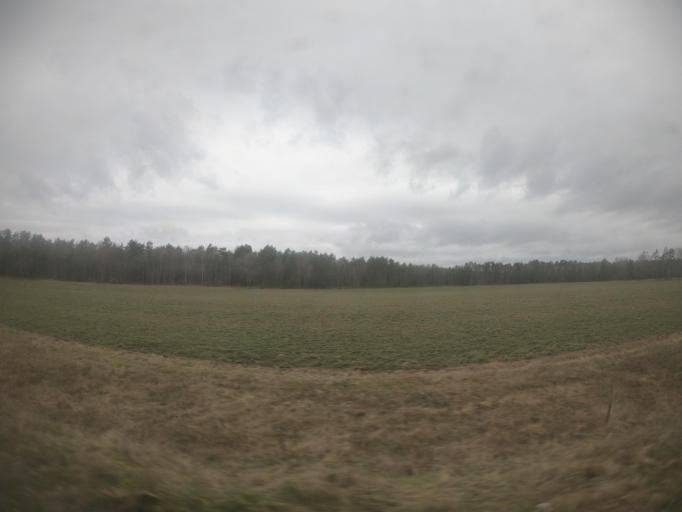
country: PL
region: West Pomeranian Voivodeship
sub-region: Powiat szczecinecki
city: Bialy Bor
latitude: 53.8230
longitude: 16.8709
